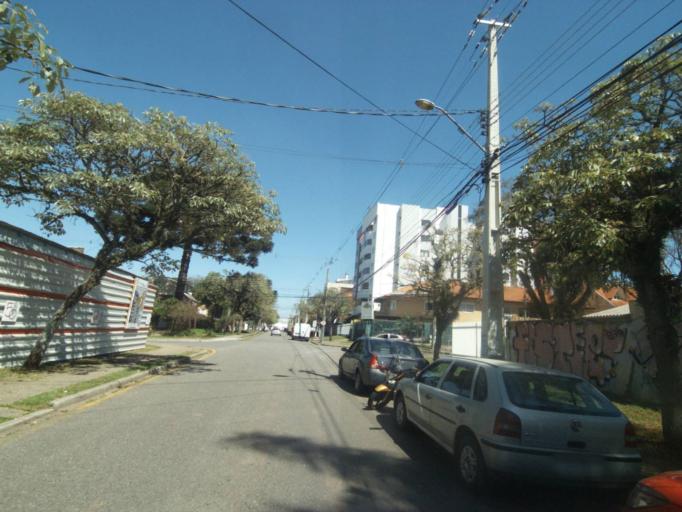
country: BR
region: Parana
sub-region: Curitiba
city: Curitiba
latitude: -25.3988
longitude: -49.2405
